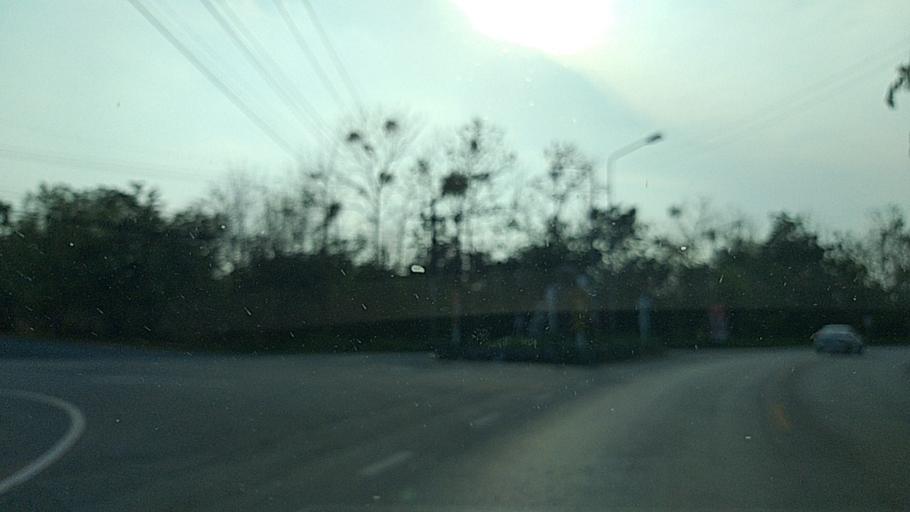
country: TH
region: Sara Buri
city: Saraburi
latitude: 14.4574
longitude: 100.9466
